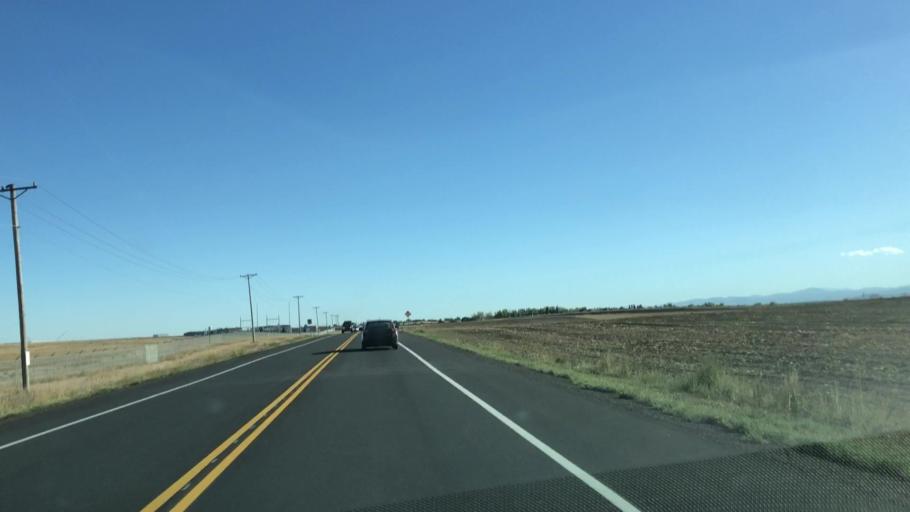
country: US
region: Colorado
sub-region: Larimer County
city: Loveland
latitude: 40.4532
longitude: -105.0205
